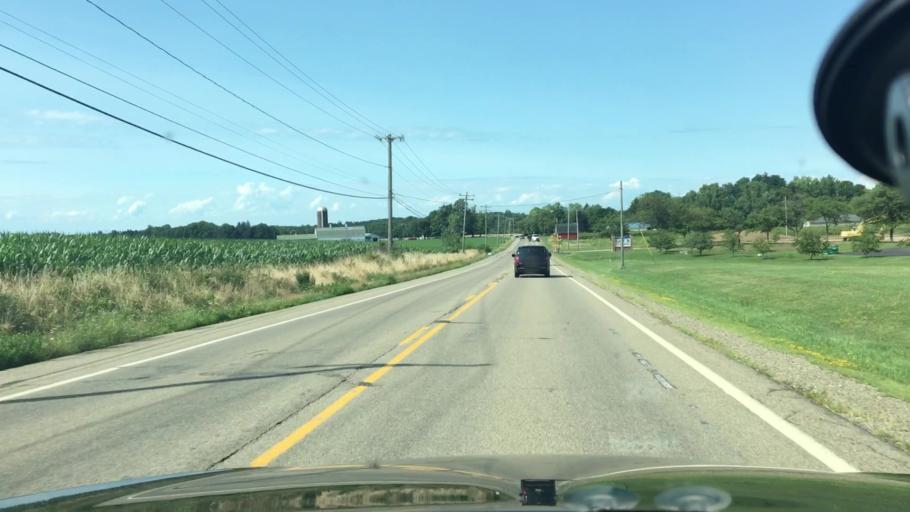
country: US
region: New York
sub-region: Chautauqua County
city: Fredonia
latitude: 42.4157
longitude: -79.3125
